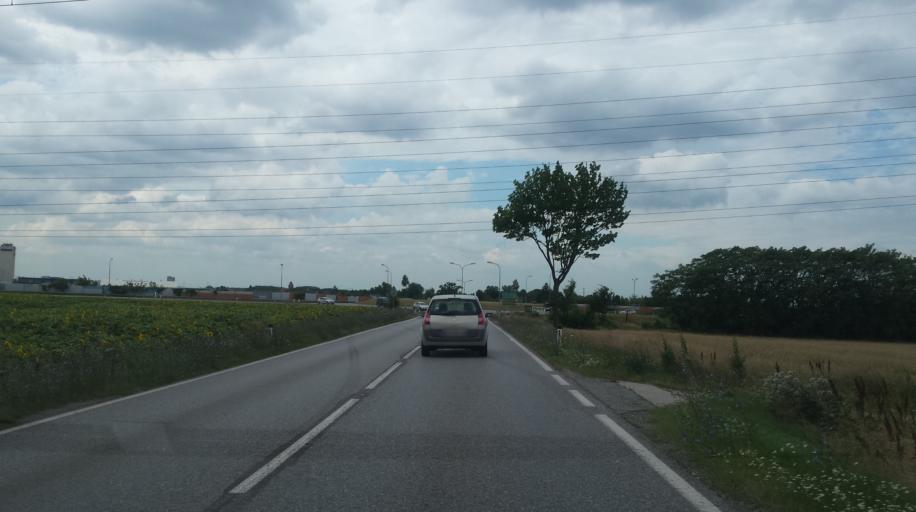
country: AT
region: Lower Austria
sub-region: Politischer Bezirk Wien-Umgebung
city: Lanzendorf
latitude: 48.0936
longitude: 16.4487
